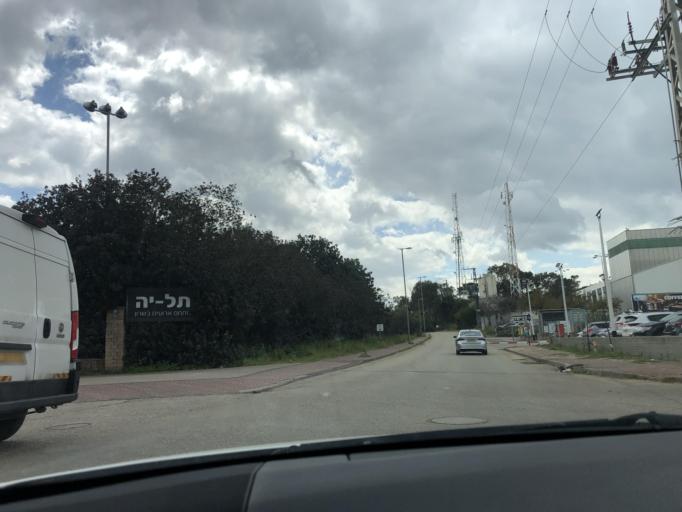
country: IL
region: Central District
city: Even Yehuda
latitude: 32.2548
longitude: 34.8733
